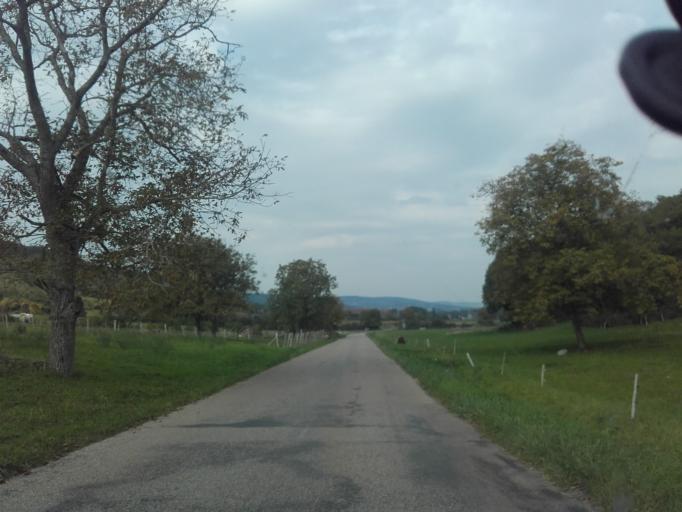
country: FR
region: Bourgogne
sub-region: Departement de Saone-et-Loire
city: Rully
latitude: 46.8876
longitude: 4.7033
